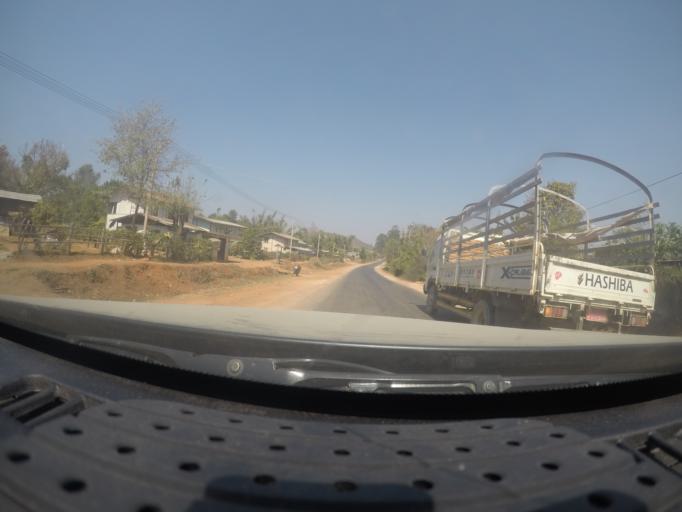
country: MM
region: Shan
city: Taunggyi
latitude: 20.8389
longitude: 96.5990
